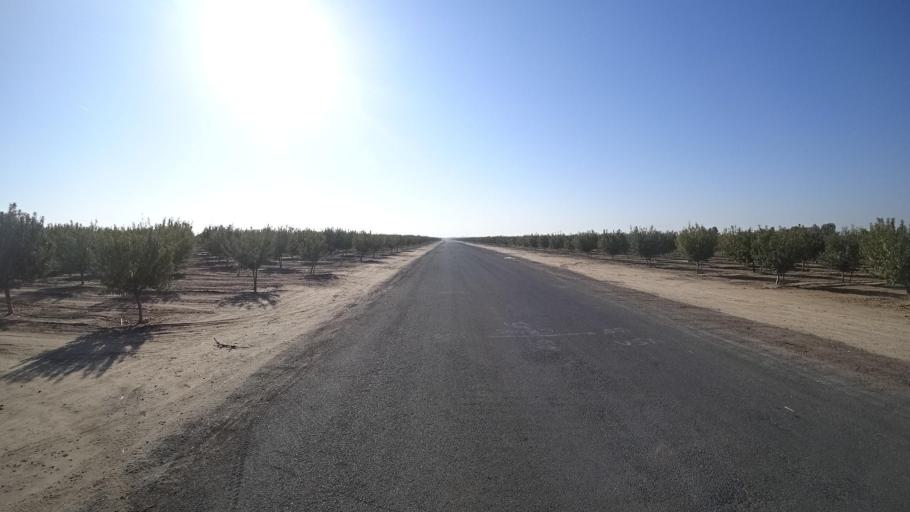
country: US
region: California
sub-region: Kern County
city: Delano
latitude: 35.7594
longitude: -119.2318
